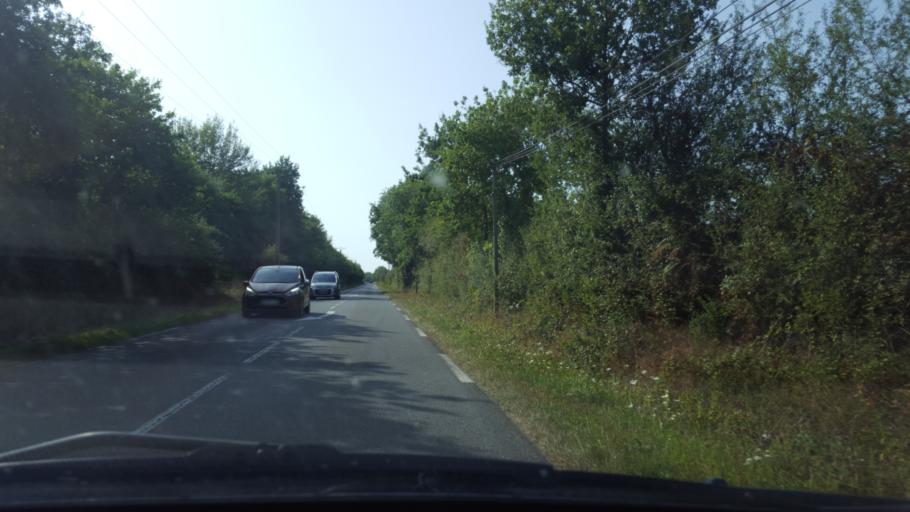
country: FR
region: Pays de la Loire
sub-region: Departement de la Loire-Atlantique
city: Geneston
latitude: 47.0607
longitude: -1.5465
